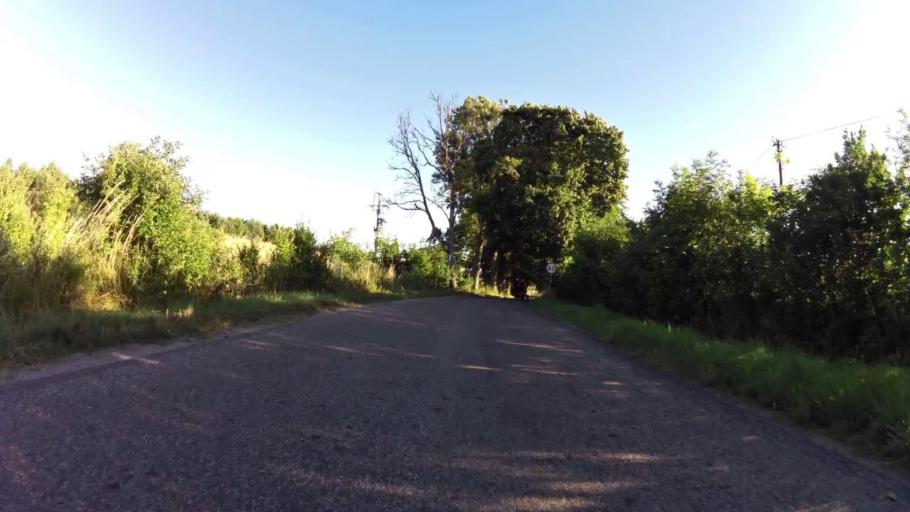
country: PL
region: West Pomeranian Voivodeship
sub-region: Powiat swidwinski
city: Swidwin
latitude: 53.7444
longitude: 15.6876
